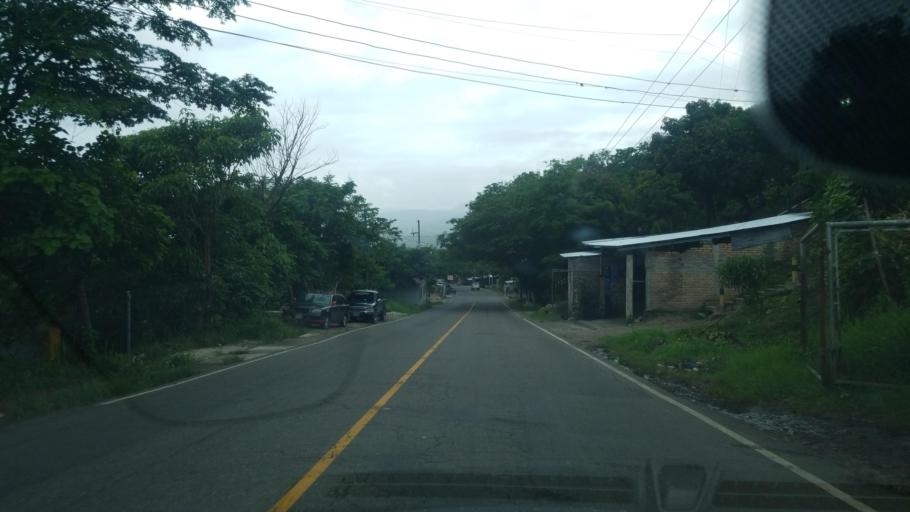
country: HN
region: Ocotepeque
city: Sinuapa
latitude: 14.4488
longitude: -89.1715
